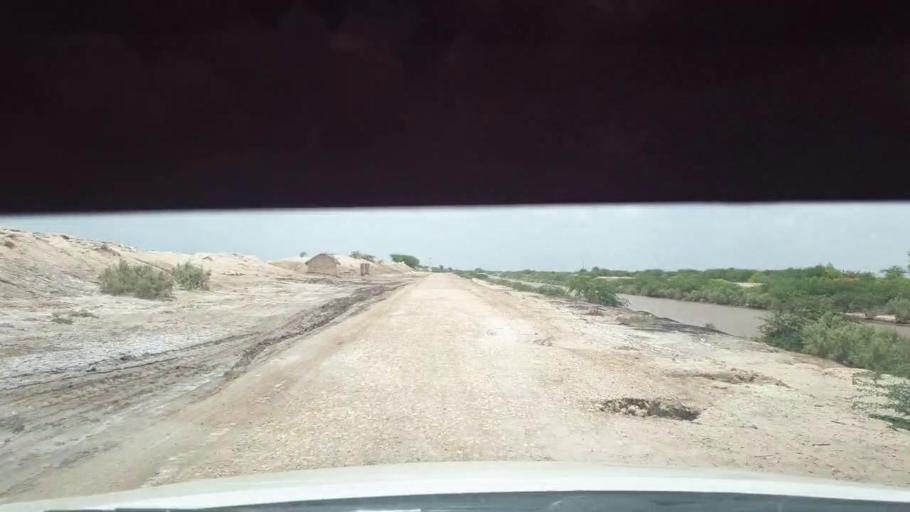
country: PK
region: Sindh
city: Kadhan
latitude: 24.5170
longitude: 69.1208
